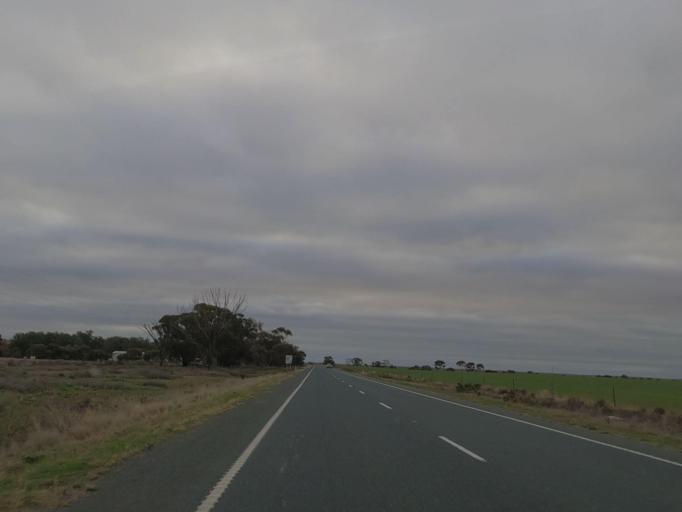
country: AU
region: Victoria
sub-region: Swan Hill
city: Swan Hill
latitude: -35.5604
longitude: 143.7809
